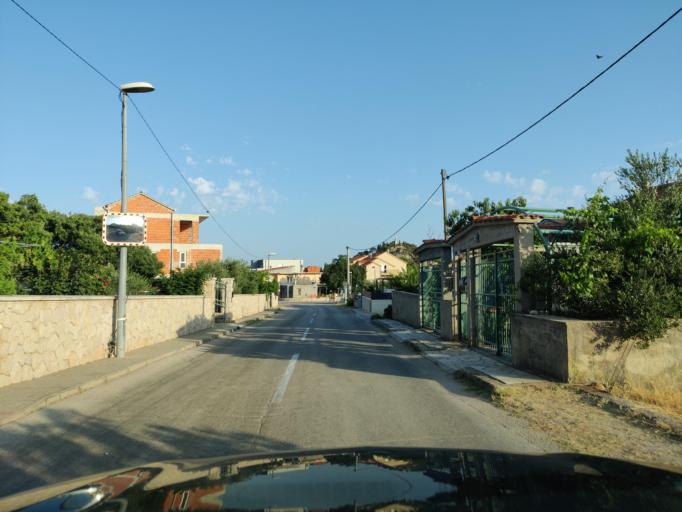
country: HR
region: Sibensko-Kniniska
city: Tribunj
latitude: 43.7607
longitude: 15.7400
